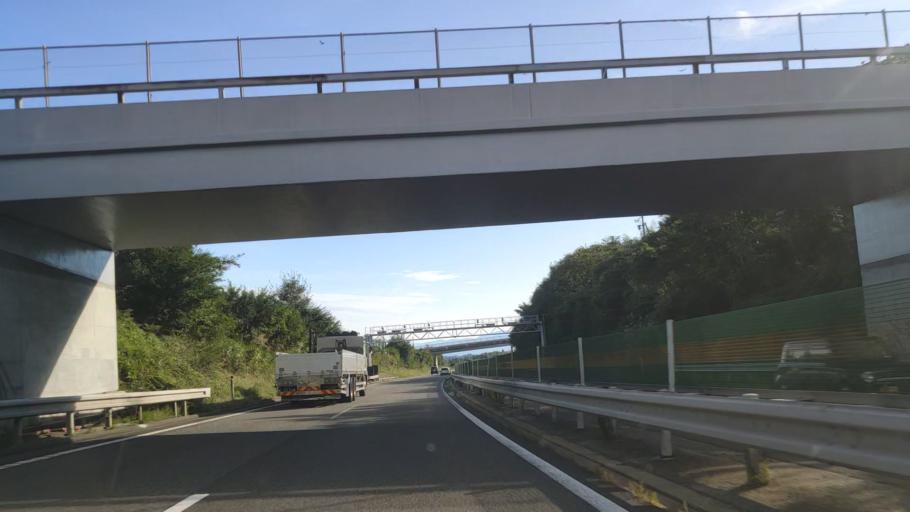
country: JP
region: Nagano
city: Iida
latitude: 35.5857
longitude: 137.8819
